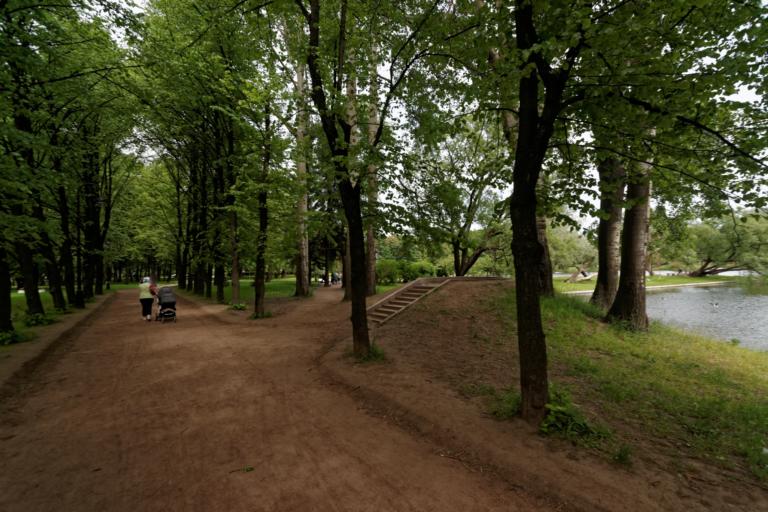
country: RU
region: St.-Petersburg
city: Kupchino
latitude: 59.8678
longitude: 30.3232
